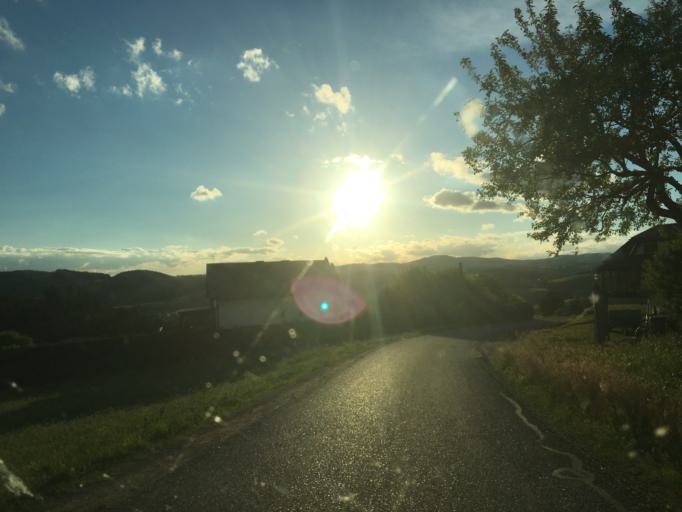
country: AT
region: Upper Austria
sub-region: Politischer Bezirk Urfahr-Umgebung
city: Zwettl an der Rodl
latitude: 48.4597
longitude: 14.2860
